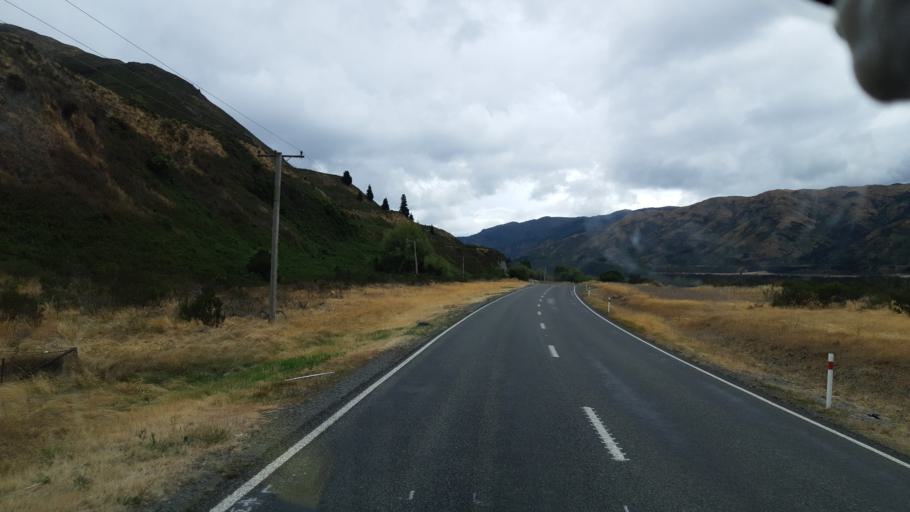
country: NZ
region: Canterbury
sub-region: Hurunui District
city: Amberley
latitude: -42.5697
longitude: 172.6915
